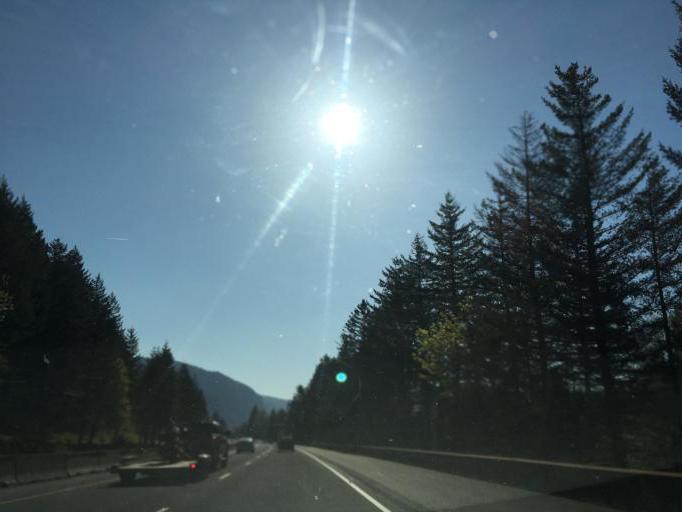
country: US
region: Oregon
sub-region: Hood River County
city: Cascade Locks
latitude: 45.6093
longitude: -122.0299
